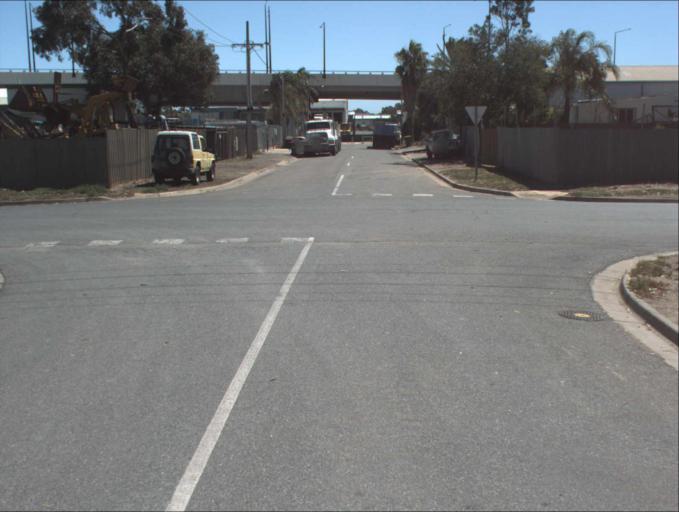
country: AU
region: South Australia
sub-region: Port Adelaide Enfield
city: Blair Athol
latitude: -34.8357
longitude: 138.5647
